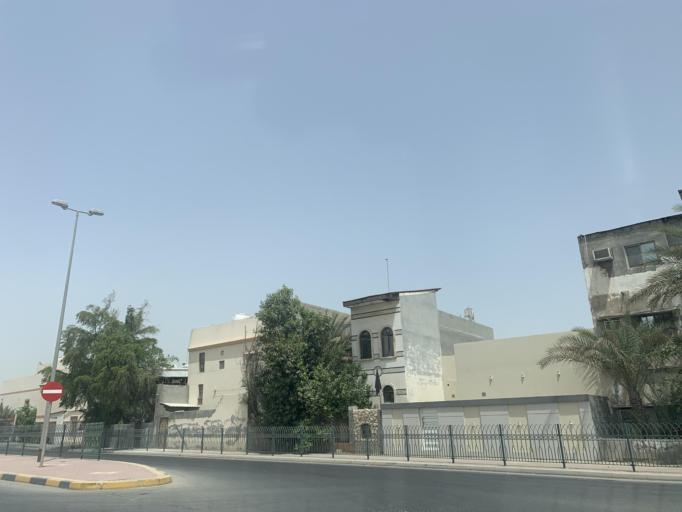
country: BH
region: Northern
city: Madinat `Isa
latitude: 26.1520
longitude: 50.5192
